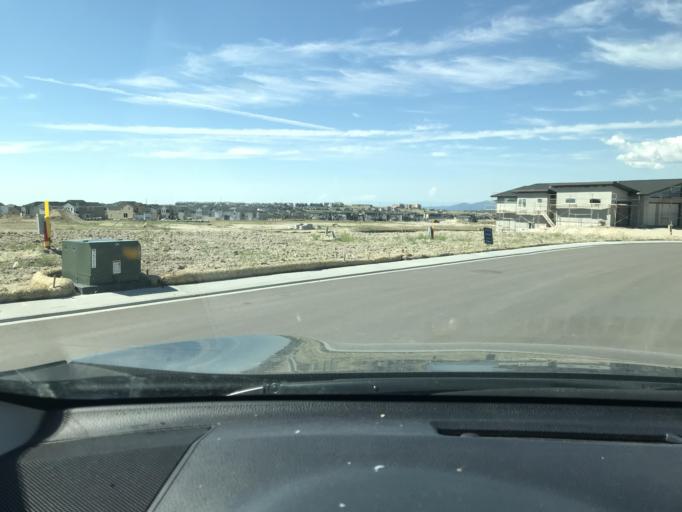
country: US
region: Colorado
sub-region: El Paso County
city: Black Forest
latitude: 38.9653
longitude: -104.7072
